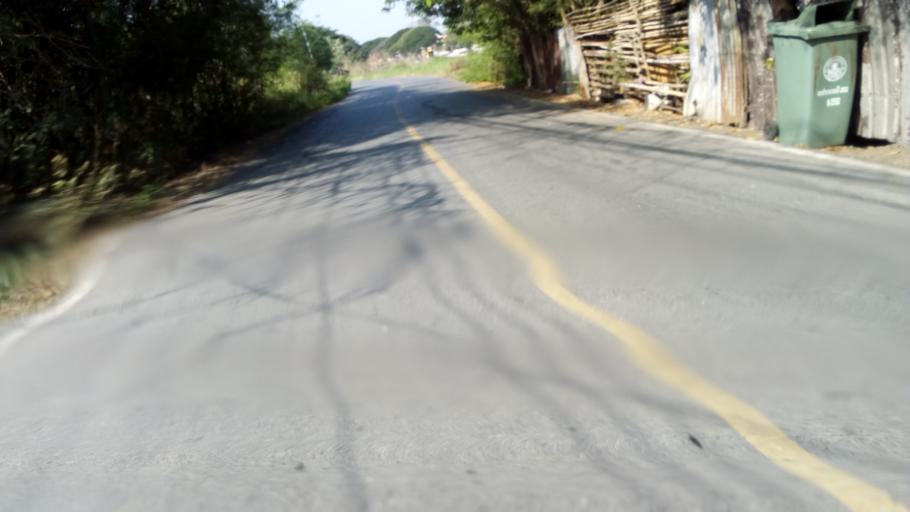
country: TH
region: Pathum Thani
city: Nong Suea
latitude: 14.0555
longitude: 100.8346
